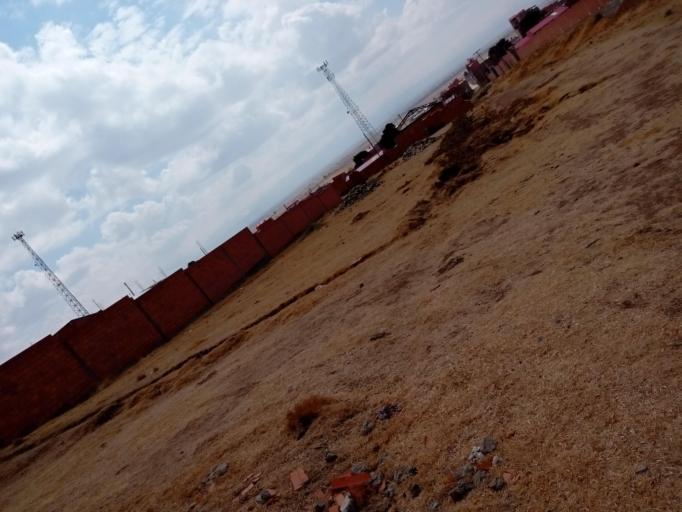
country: BO
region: La Paz
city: Batallas
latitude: -16.4010
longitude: -68.4813
